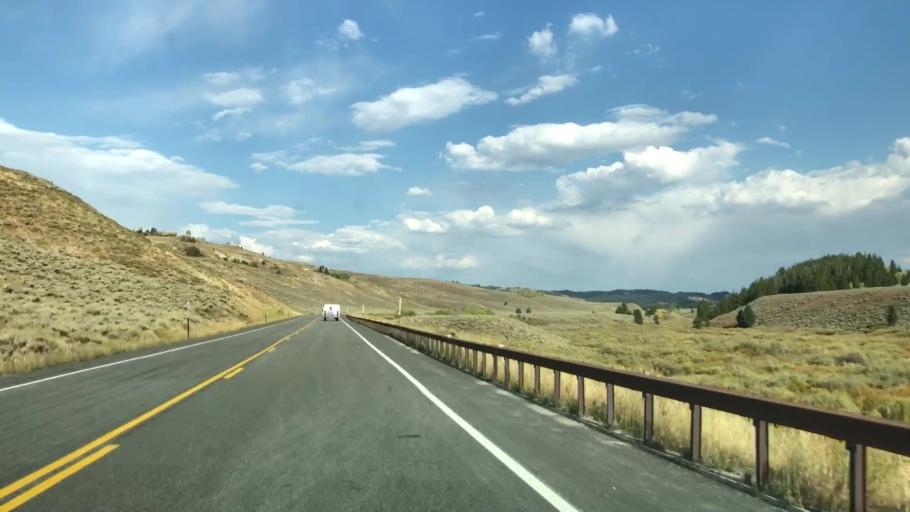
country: US
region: Wyoming
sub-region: Teton County
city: Hoback
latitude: 43.1518
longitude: -110.2877
